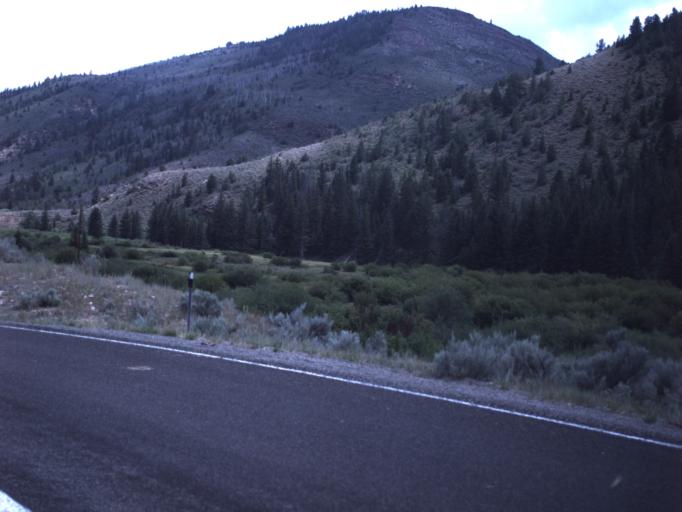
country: US
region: Utah
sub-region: Summit County
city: Francis
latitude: 40.4519
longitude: -110.8675
